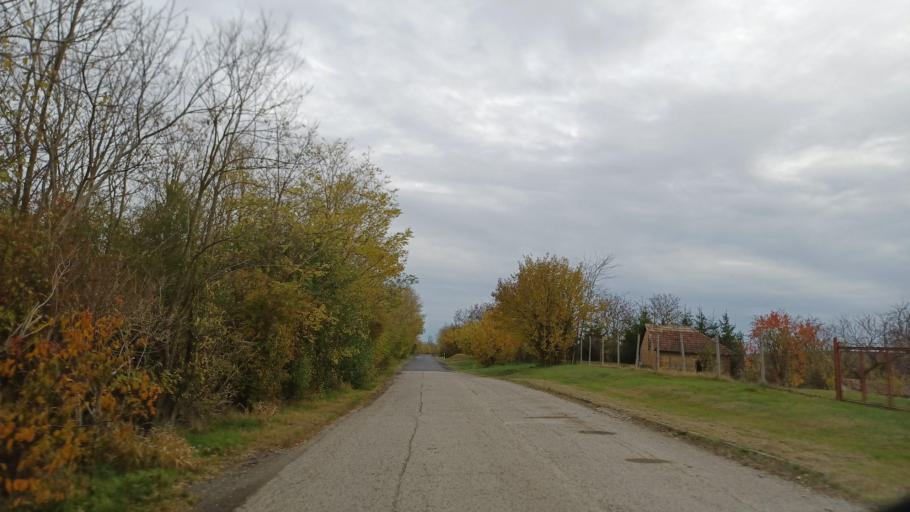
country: HU
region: Tolna
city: Simontornya
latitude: 46.6868
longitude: 18.5961
